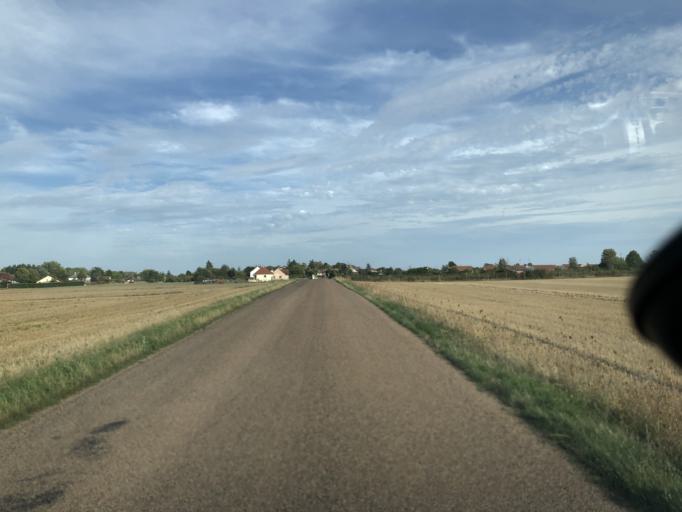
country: FR
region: Bourgogne
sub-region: Departement de l'Yonne
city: Joigny
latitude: 47.9582
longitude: 3.3931
